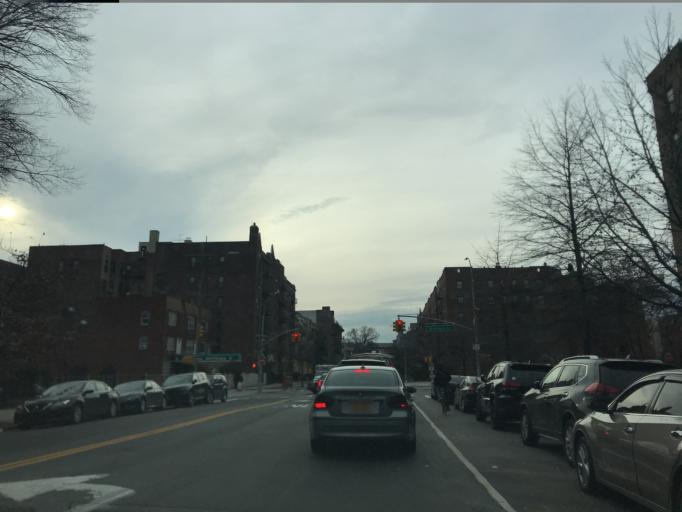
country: US
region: New York
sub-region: Kings County
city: Brooklyn
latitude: 40.6524
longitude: -73.9553
